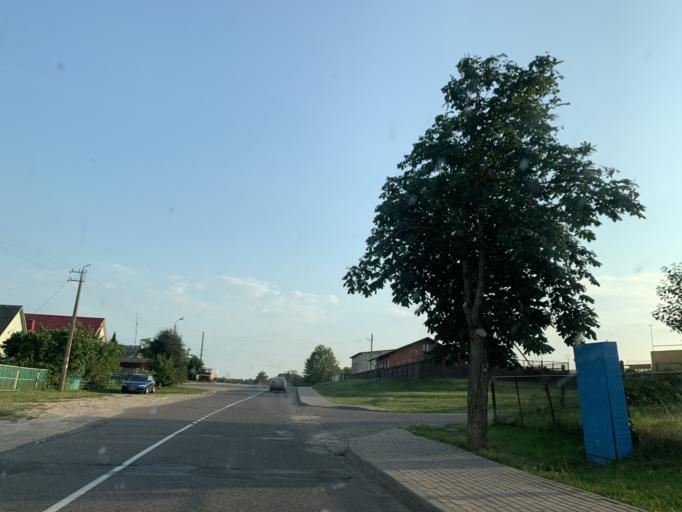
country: BY
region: Minsk
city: Nyasvizh
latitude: 53.2107
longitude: 26.6647
